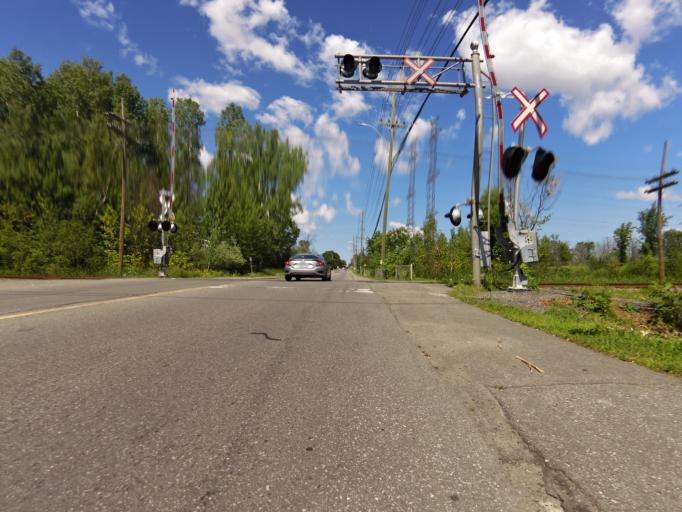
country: CA
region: Ontario
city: Ottawa
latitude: 45.3580
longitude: -75.6734
